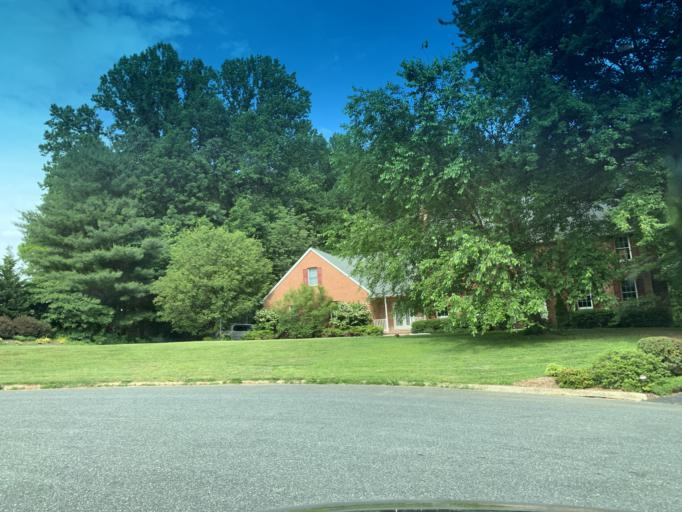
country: US
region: Maryland
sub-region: Harford County
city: Jarrettsville
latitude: 39.5967
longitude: -76.4641
